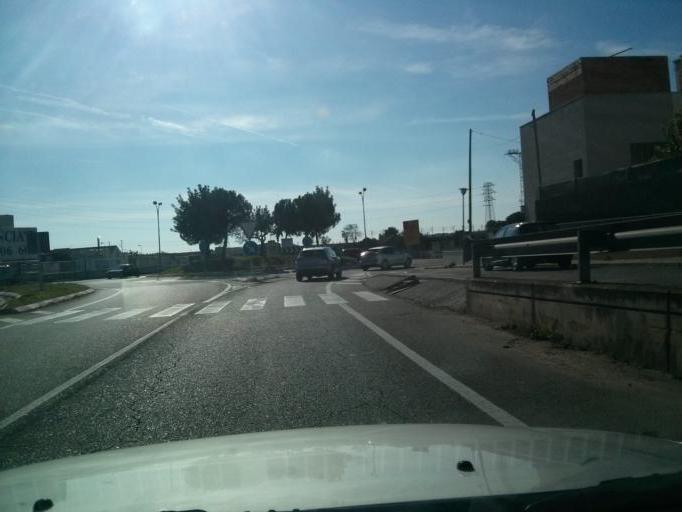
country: ES
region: Catalonia
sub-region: Provincia de Tarragona
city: Santa Oliva
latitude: 41.2364
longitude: 1.5439
